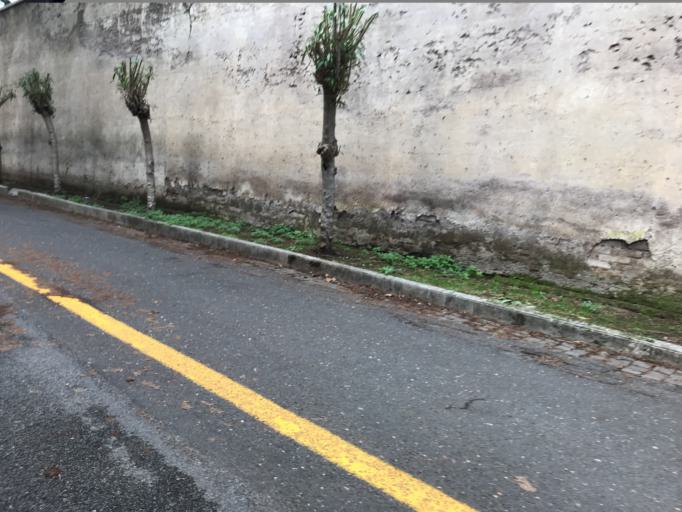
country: IT
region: Latium
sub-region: Citta metropolitana di Roma Capitale
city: Rome
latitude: 41.9079
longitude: 12.5267
